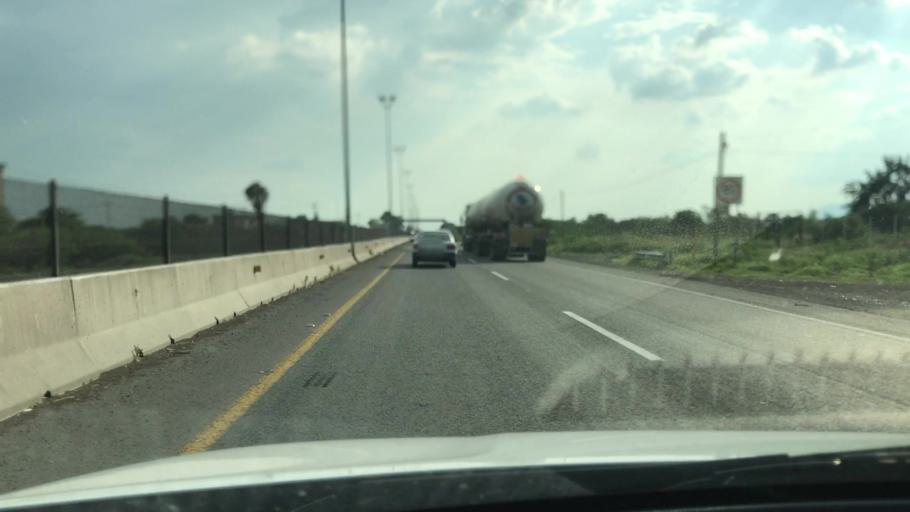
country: MX
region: Guanajuato
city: Abasolo
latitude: 20.4543
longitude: -101.5432
